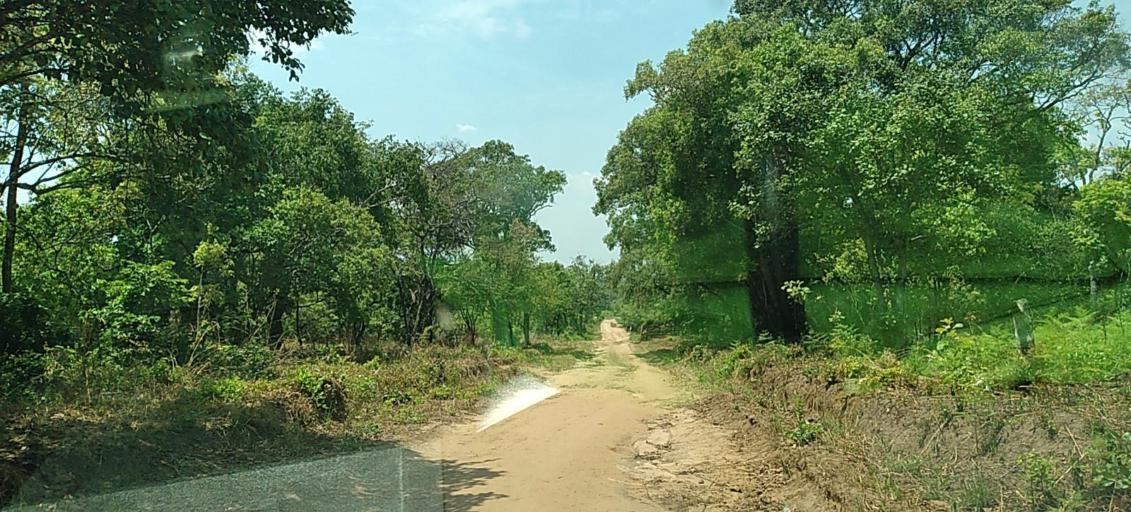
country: CD
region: Katanga
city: Kolwezi
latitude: -11.3161
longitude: 25.2342
